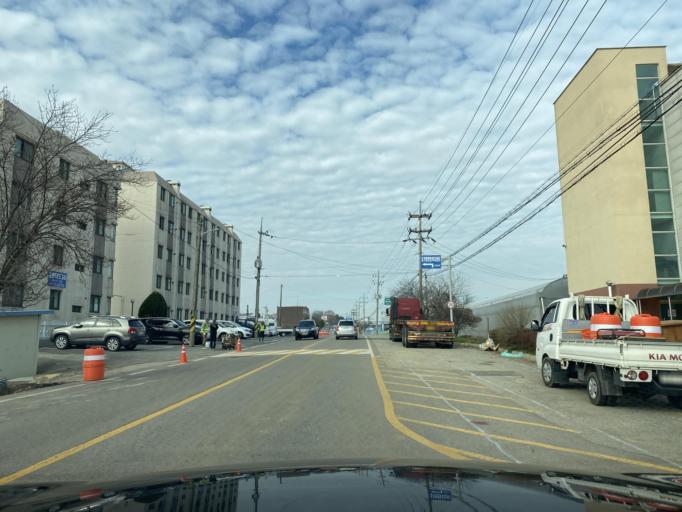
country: KR
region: Chungcheongnam-do
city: Yesan
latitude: 36.6862
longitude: 126.8015
